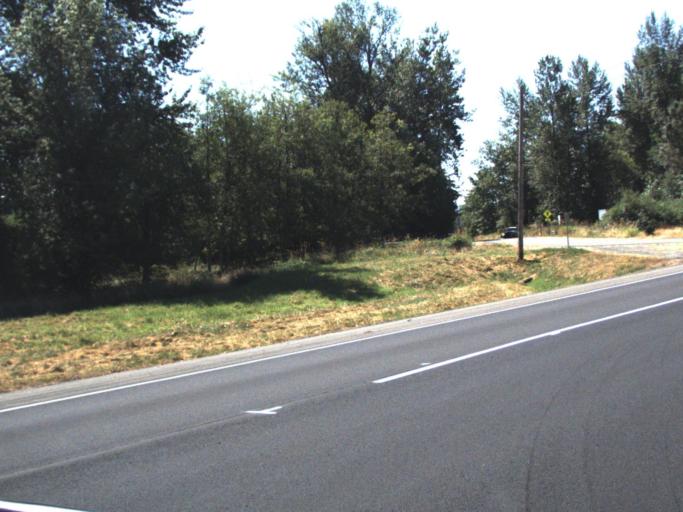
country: US
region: Washington
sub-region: King County
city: Enumclaw
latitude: 47.1872
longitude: -122.0053
